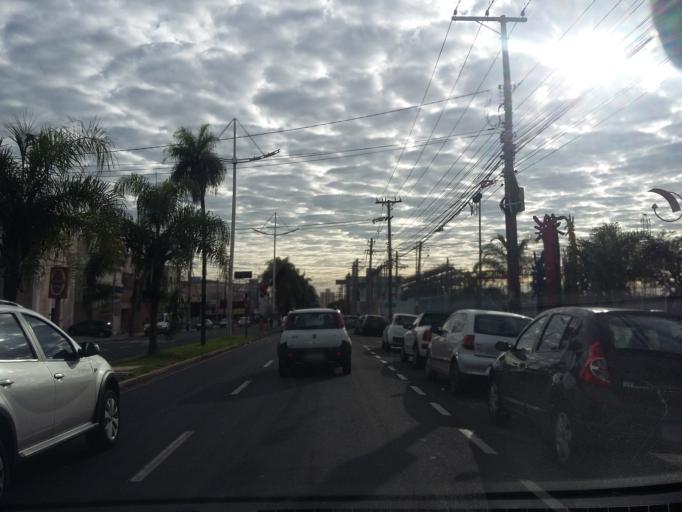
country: BR
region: Sao Paulo
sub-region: Sao Jose Do Rio Preto
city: Sao Jose do Rio Preto
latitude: -20.8278
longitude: -49.3960
